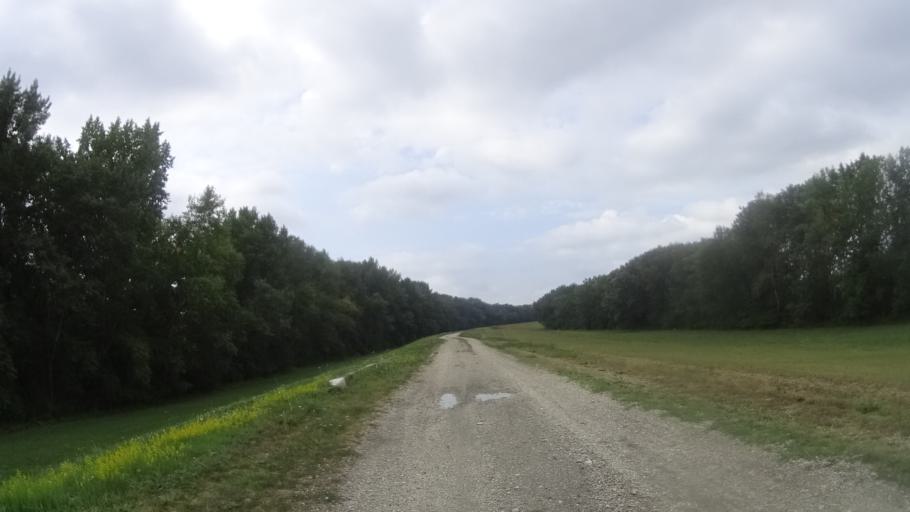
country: HU
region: Komarom-Esztergom
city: Acs
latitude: 47.7500
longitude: 17.9132
